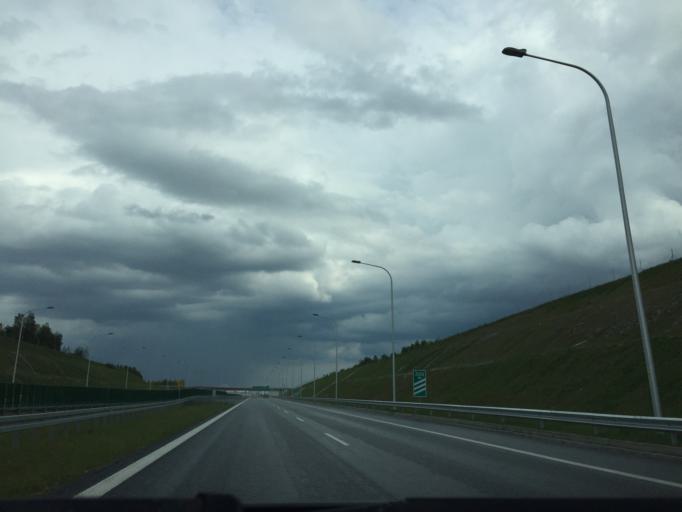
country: PL
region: Masovian Voivodeship
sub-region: Powiat szydlowiecki
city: Jastrzab
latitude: 51.2539
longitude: 20.9084
